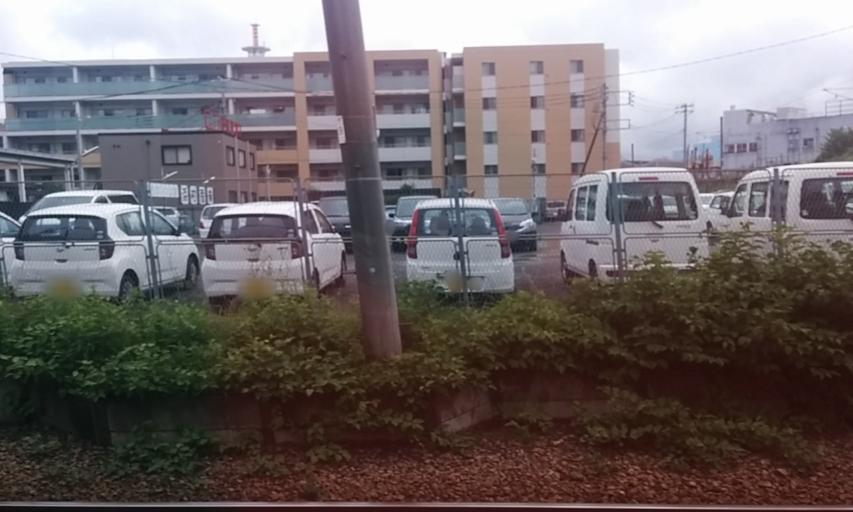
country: JP
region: Tokyo
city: Hachioji
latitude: 35.6545
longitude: 139.3471
